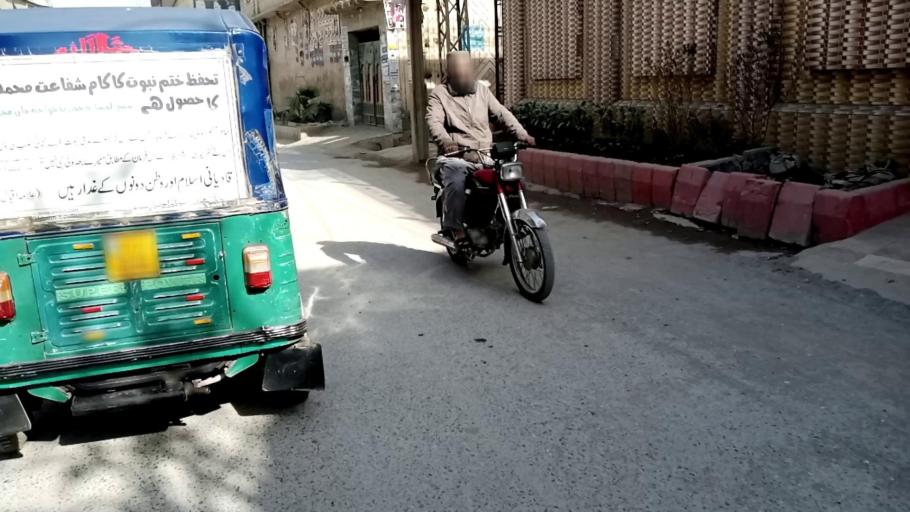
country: PK
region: Khyber Pakhtunkhwa
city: Peshawar
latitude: 34.0007
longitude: 71.5784
